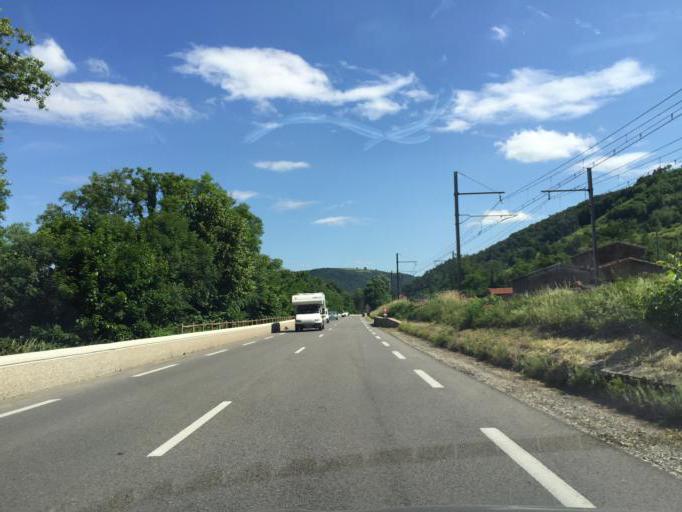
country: FR
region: Rhone-Alpes
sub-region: Departement de la Drome
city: Saint-Vallier
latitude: 45.1658
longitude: 4.8081
